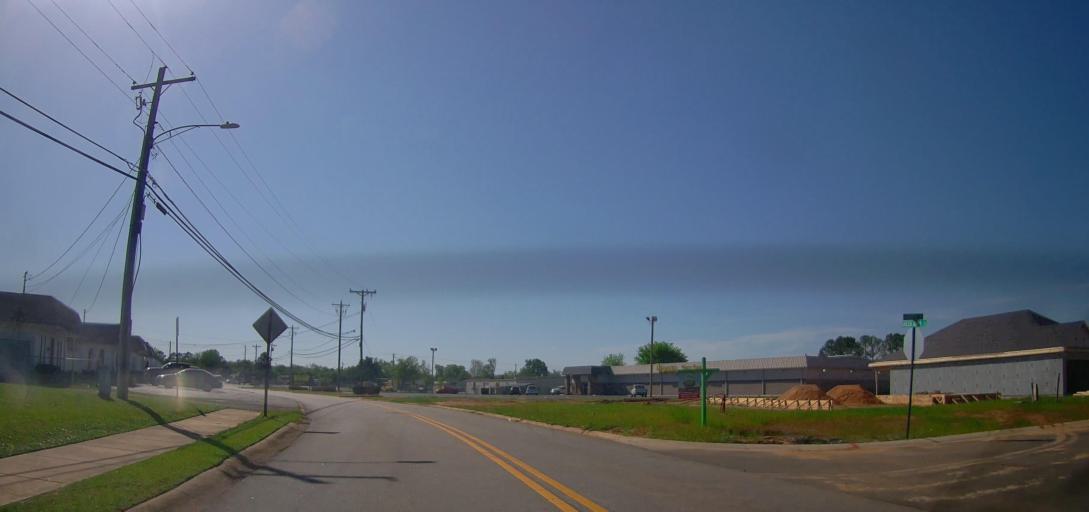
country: US
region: Georgia
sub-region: Houston County
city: Warner Robins
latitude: 32.6412
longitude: -83.6394
